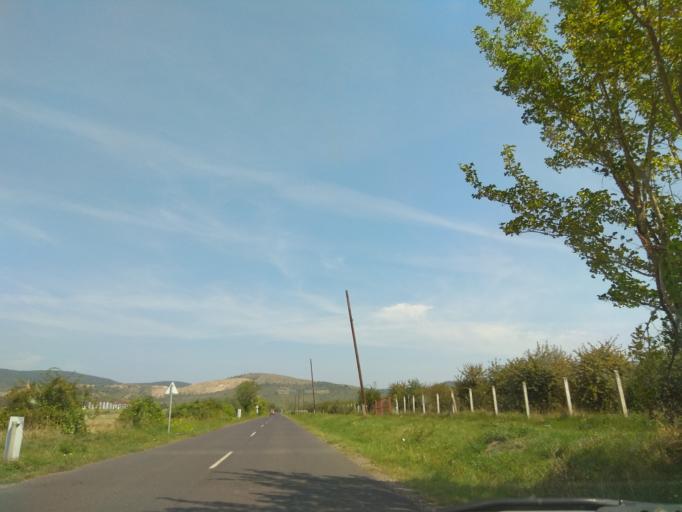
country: HU
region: Borsod-Abauj-Zemplen
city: Tallya
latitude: 48.2234
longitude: 21.2296
